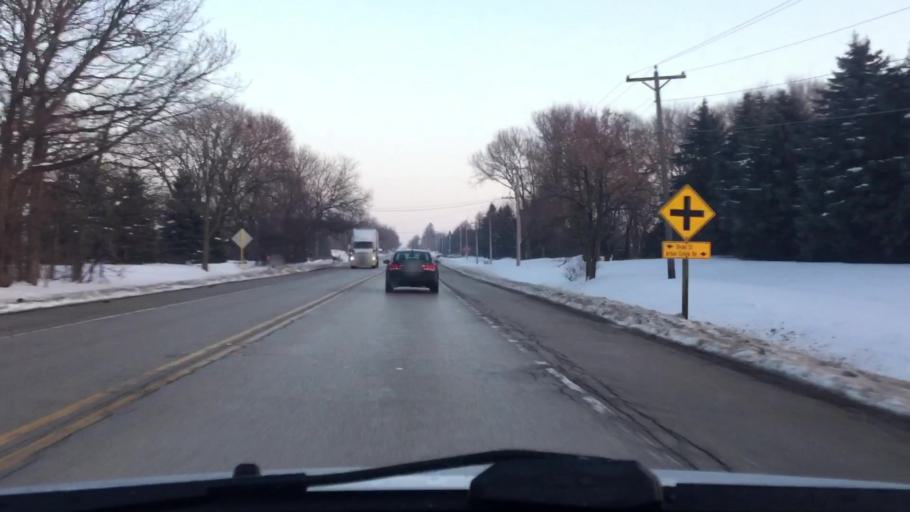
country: US
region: Illinois
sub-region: Kane County
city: Village of Campton Hills
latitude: 41.9313
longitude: -88.3803
